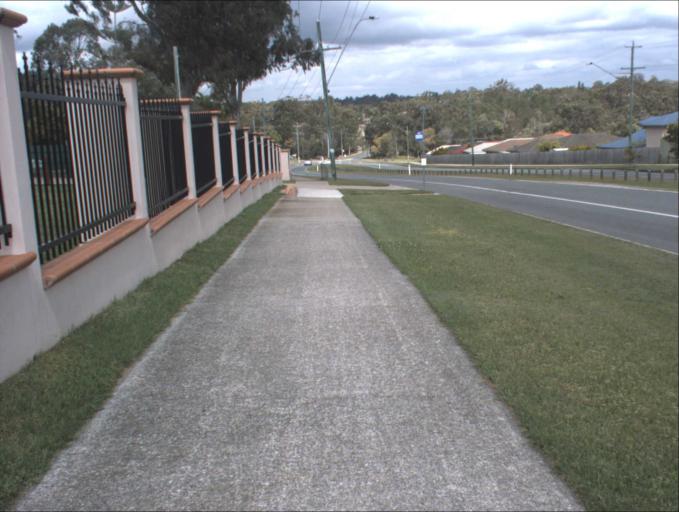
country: AU
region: Queensland
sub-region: Logan
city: Park Ridge South
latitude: -27.6832
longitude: 153.0591
